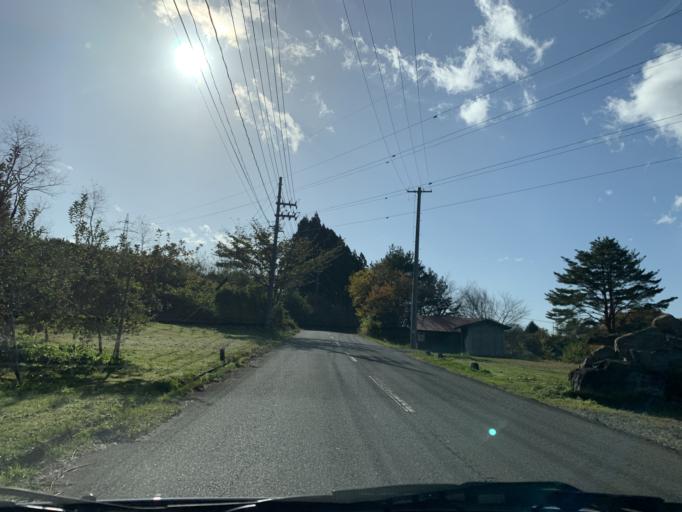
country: JP
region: Iwate
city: Mizusawa
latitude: 39.0623
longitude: 141.1208
